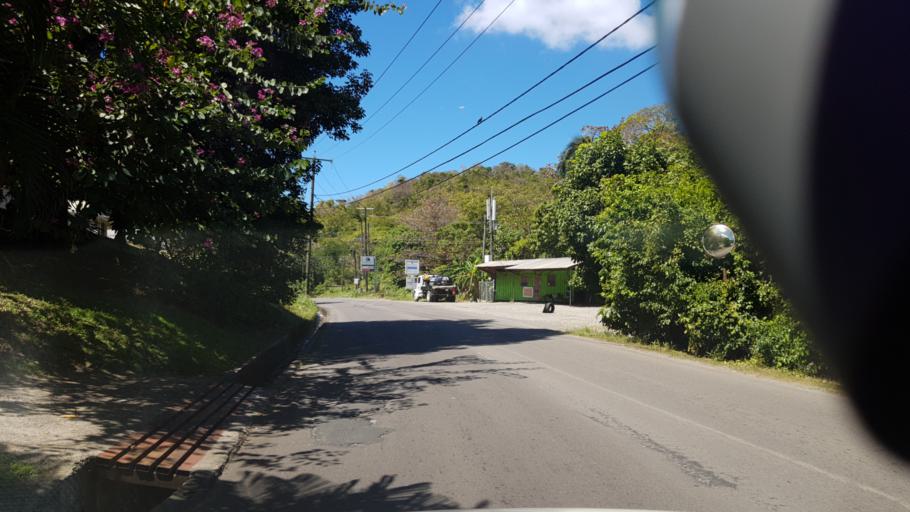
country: LC
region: Castries Quarter
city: Bisee
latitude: 14.0309
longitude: -60.9645
